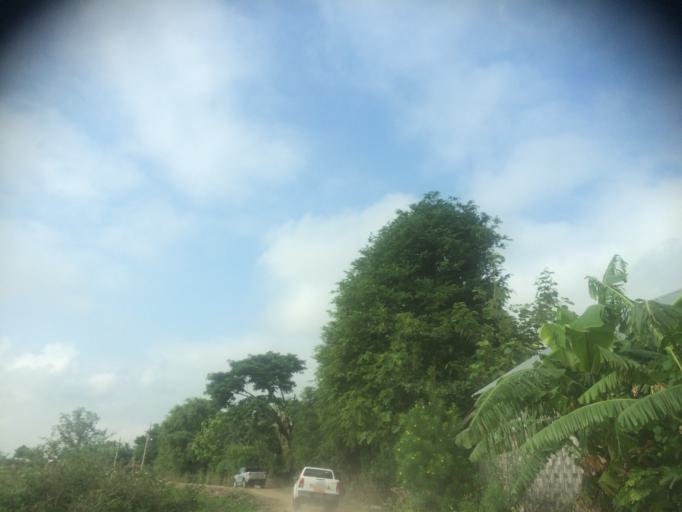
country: MM
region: Bago
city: Pyay
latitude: 18.6793
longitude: 95.0510
